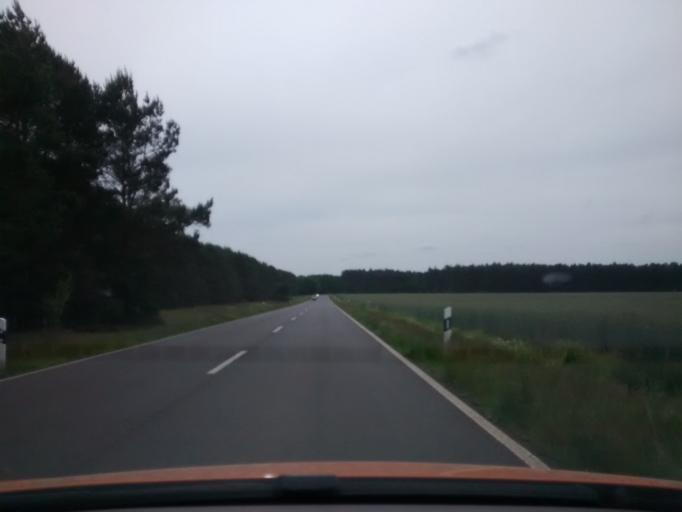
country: DE
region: Saxony-Anhalt
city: Holzdorf
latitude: 51.8572
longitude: 13.1468
